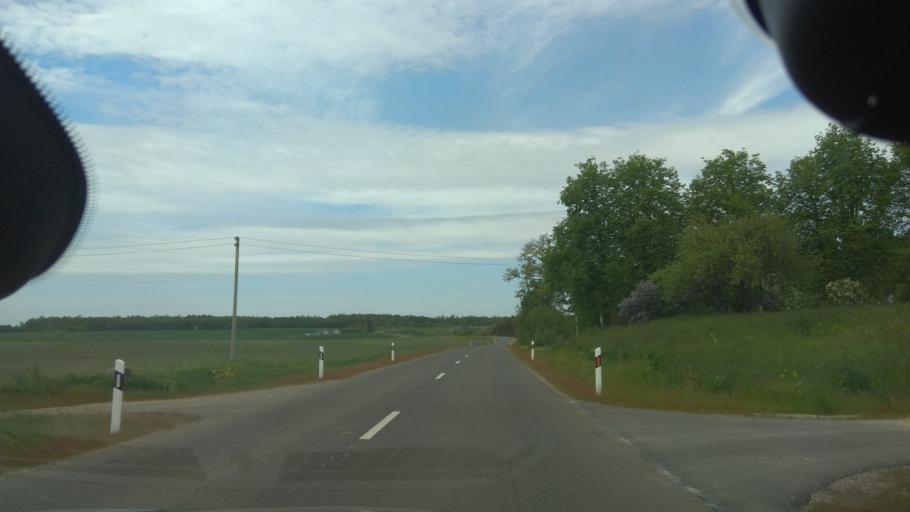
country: LT
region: Vilnius County
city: Ukmerge
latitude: 55.1068
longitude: 24.6754
